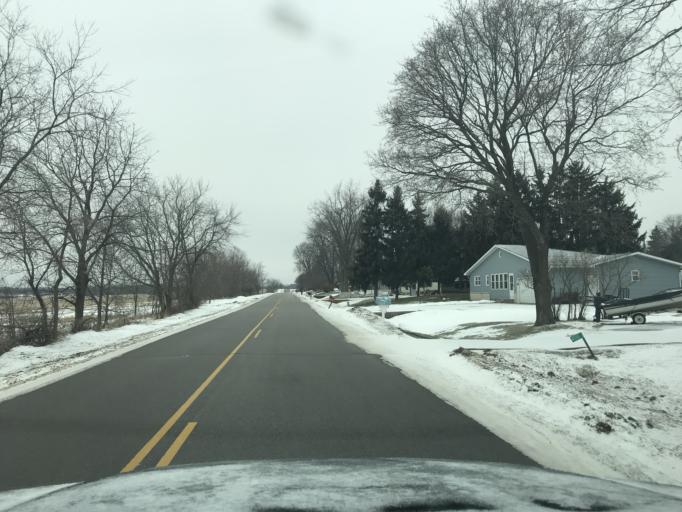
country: US
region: Wisconsin
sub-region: Dane County
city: Cottage Grove
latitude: 43.0942
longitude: -89.2361
